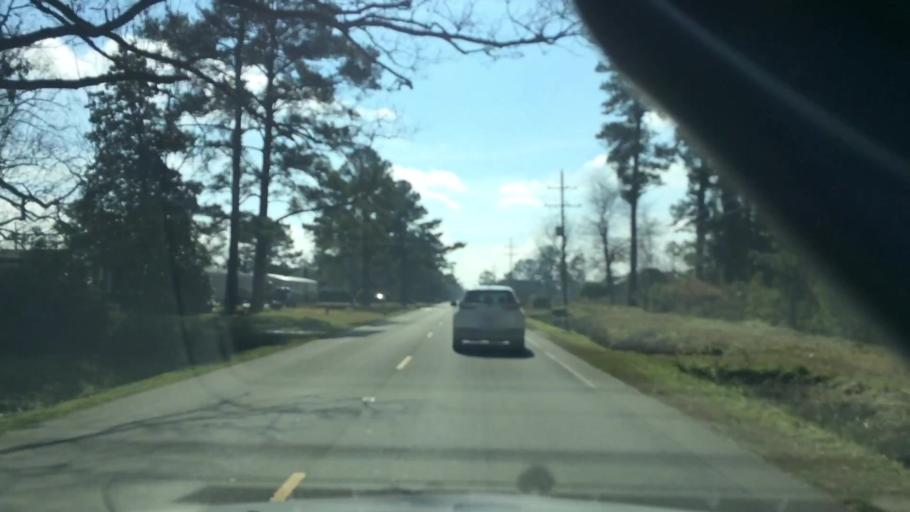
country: US
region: North Carolina
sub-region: Duplin County
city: Beulaville
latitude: 34.8964
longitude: -77.7817
